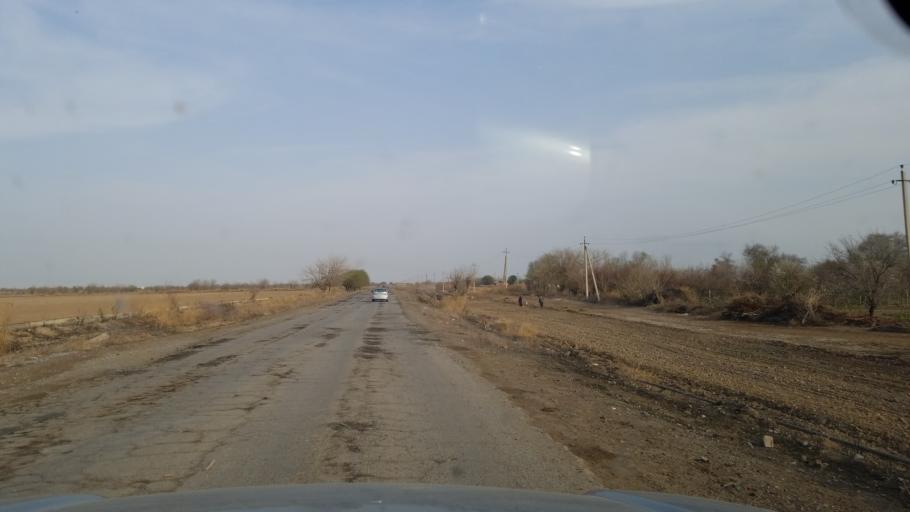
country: TM
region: Mary
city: Bayramaly
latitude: 37.6168
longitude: 62.2288
